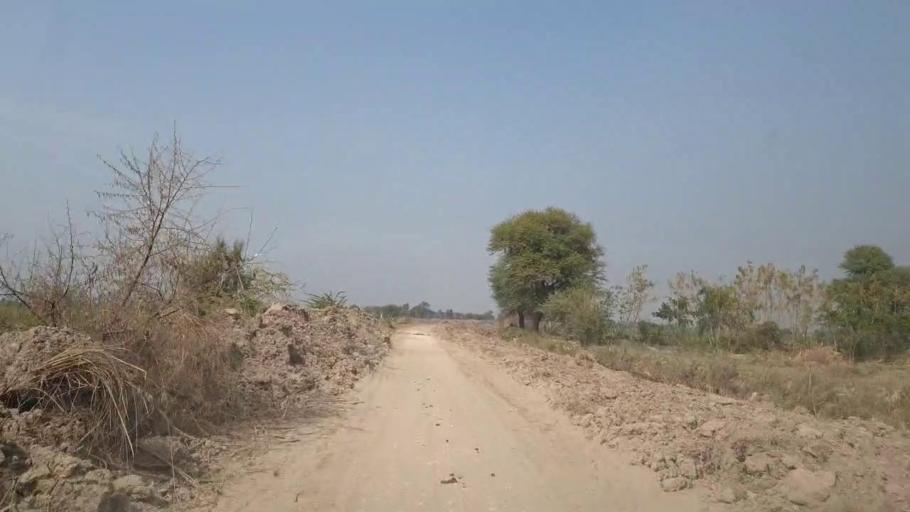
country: PK
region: Sindh
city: Mirpur Khas
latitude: 25.5645
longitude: 69.1433
